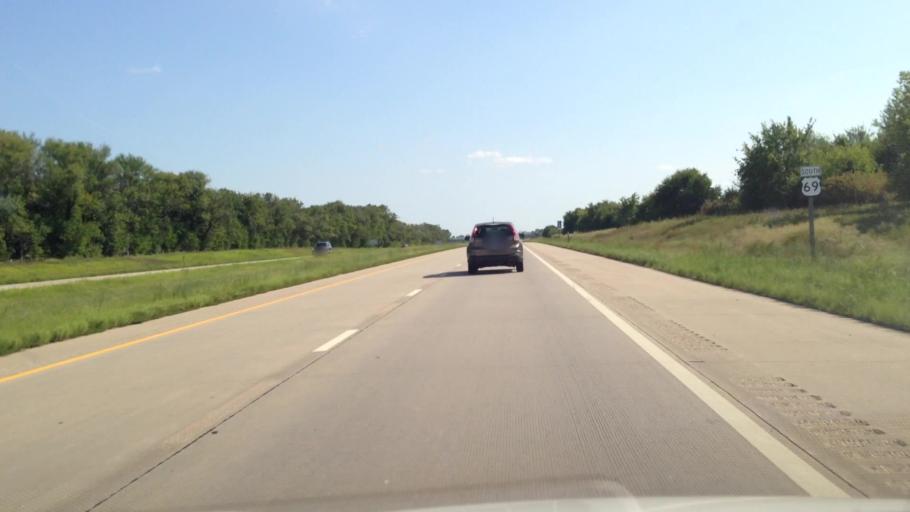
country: US
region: Kansas
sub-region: Bourbon County
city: Fort Scott
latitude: 37.9872
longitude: -94.7048
